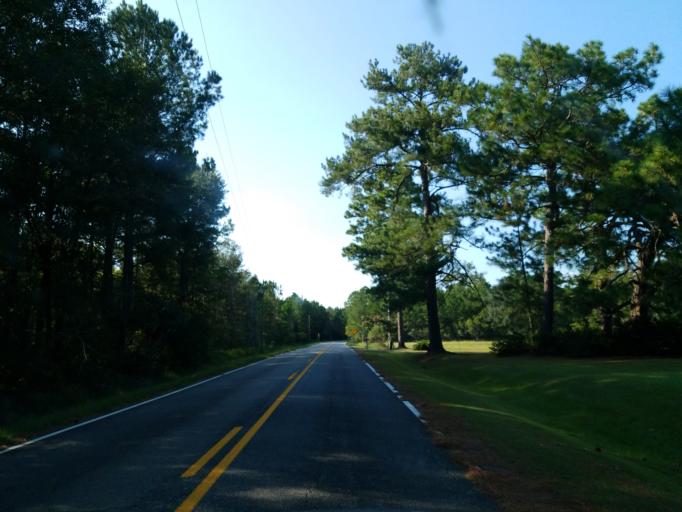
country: US
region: Georgia
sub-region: Lowndes County
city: Hahira
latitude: 31.0265
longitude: -83.3912
